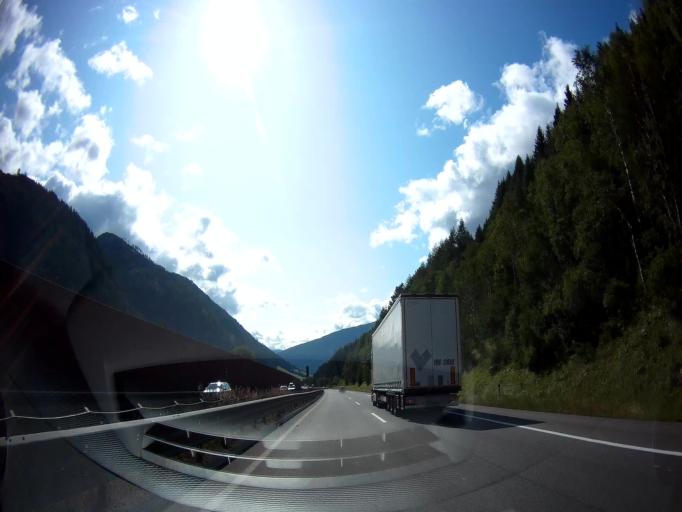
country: AT
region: Salzburg
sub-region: Politischer Bezirk Tamsweg
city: Tweng
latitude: 47.1231
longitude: 13.5655
